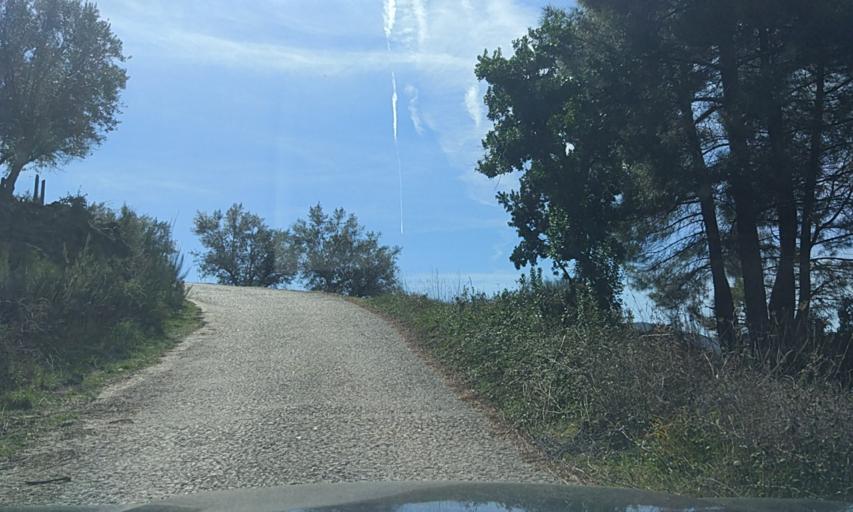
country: PT
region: Vila Real
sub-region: Sabrosa
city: Sabrosa
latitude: 41.3029
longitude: -7.5468
